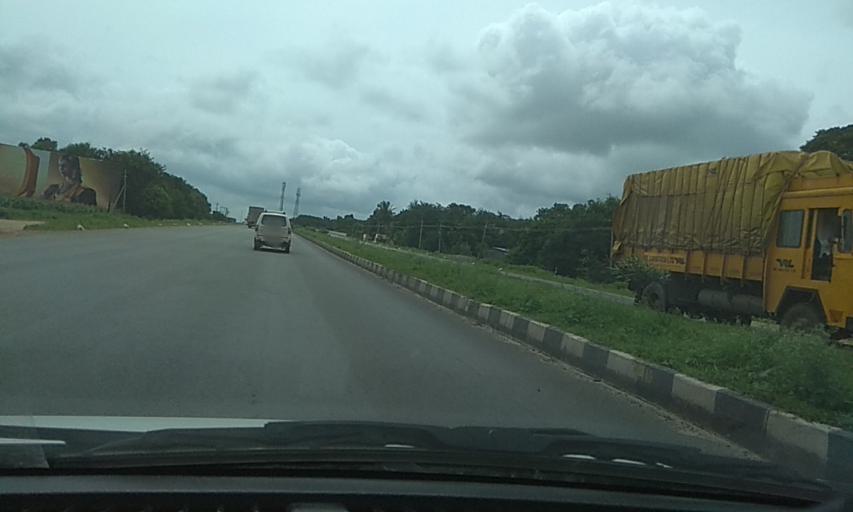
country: IN
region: Karnataka
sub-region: Davanagere
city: Mayakonda
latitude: 14.3790
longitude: 76.0936
